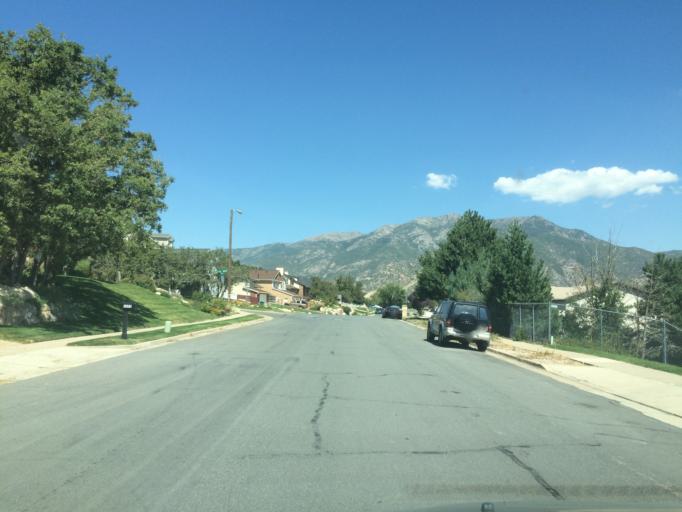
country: US
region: Utah
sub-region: Davis County
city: South Weber
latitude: 41.1101
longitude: -111.9188
